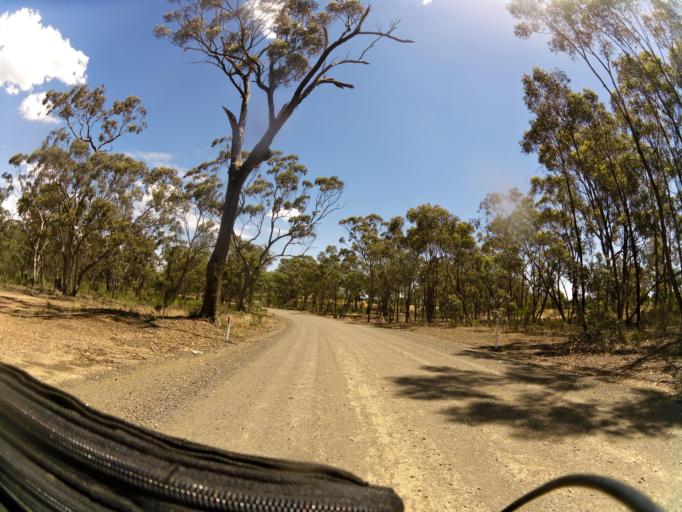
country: AU
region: Victoria
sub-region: Campaspe
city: Kyabram
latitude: -36.8051
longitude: 145.0728
